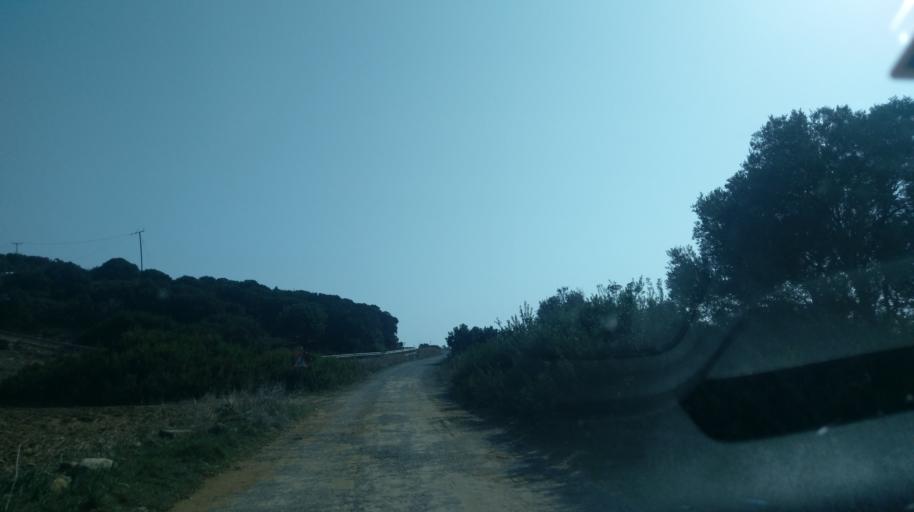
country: CY
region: Ammochostos
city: Rizokarpaso
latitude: 35.6465
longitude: 34.5533
